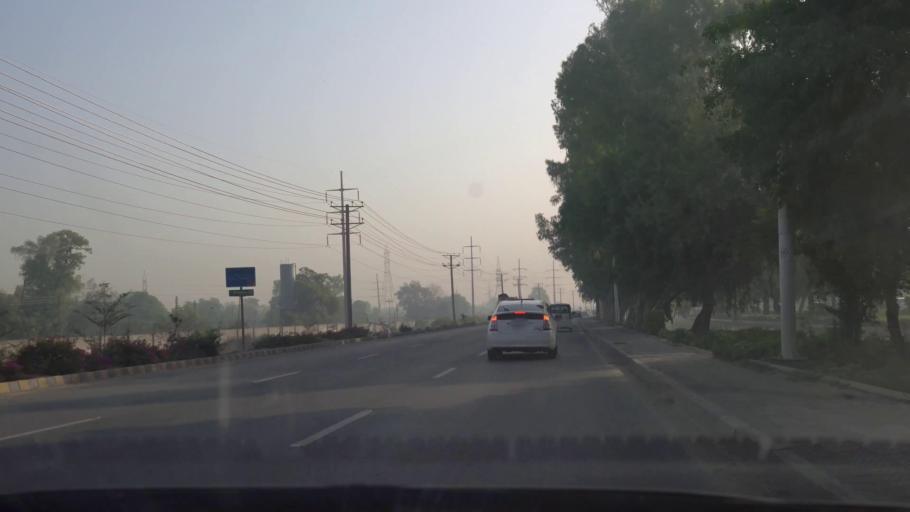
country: PK
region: Punjab
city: Faisalabad
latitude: 31.4477
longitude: 73.1434
